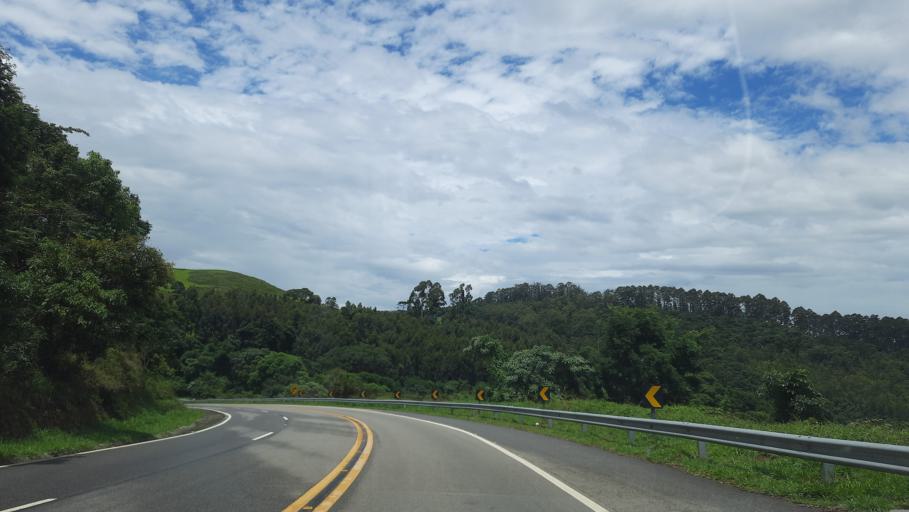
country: BR
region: Minas Gerais
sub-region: Pocos De Caldas
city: Pocos de Caldas
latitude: -21.8452
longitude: -46.6990
